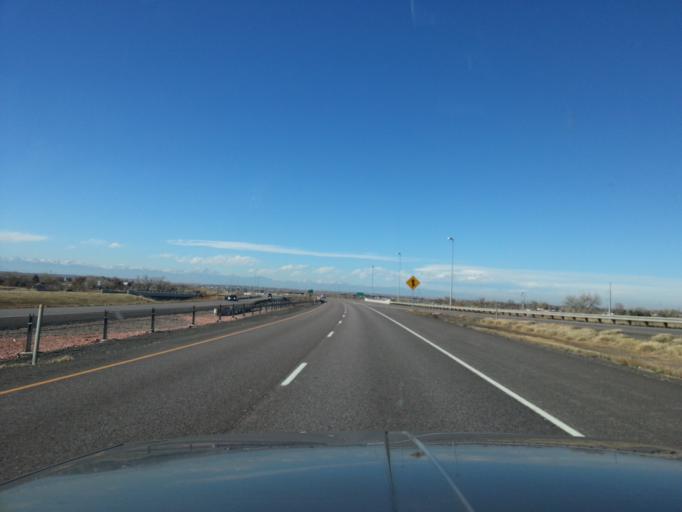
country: US
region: Colorado
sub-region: Adams County
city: Brighton
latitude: 39.9169
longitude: -104.7847
